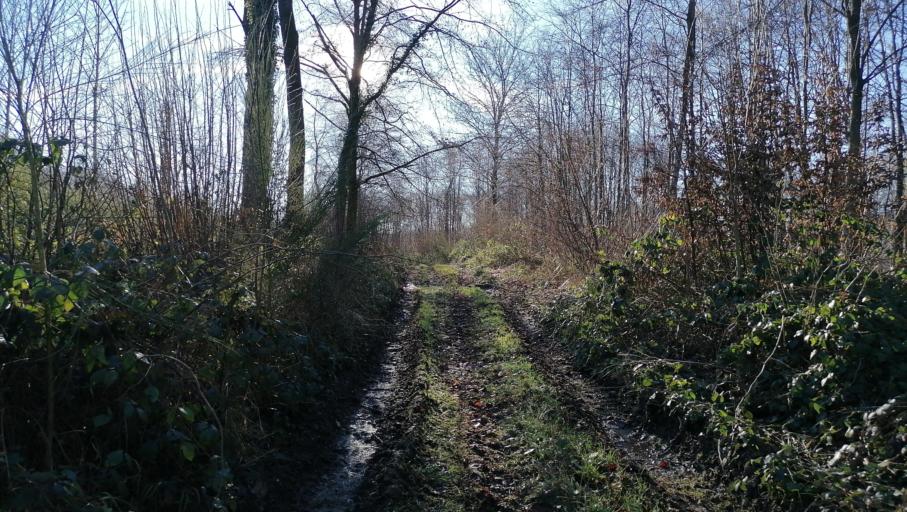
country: FR
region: Nord-Pas-de-Calais
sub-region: Departement du Nord
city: Recquignies
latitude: 50.1984
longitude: 4.0676
